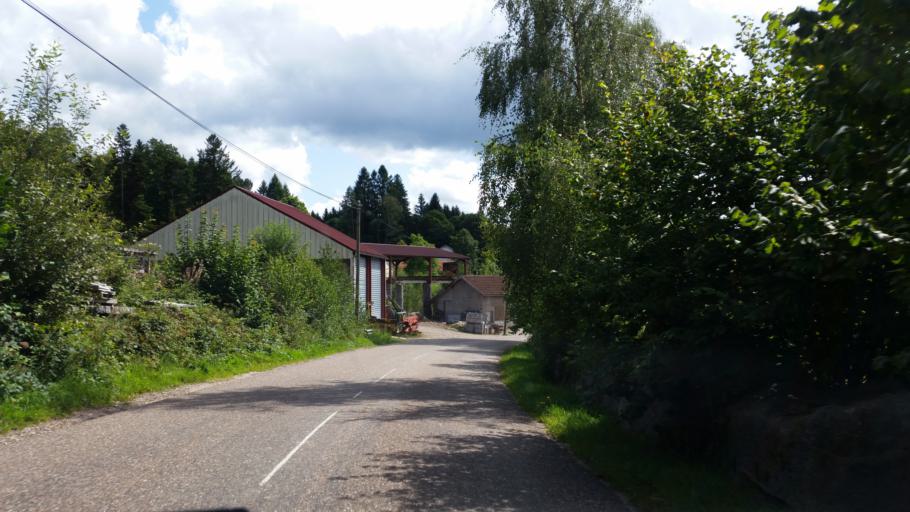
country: FR
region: Lorraine
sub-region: Departement des Vosges
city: Le Tholy
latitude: 48.0974
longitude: 6.7698
